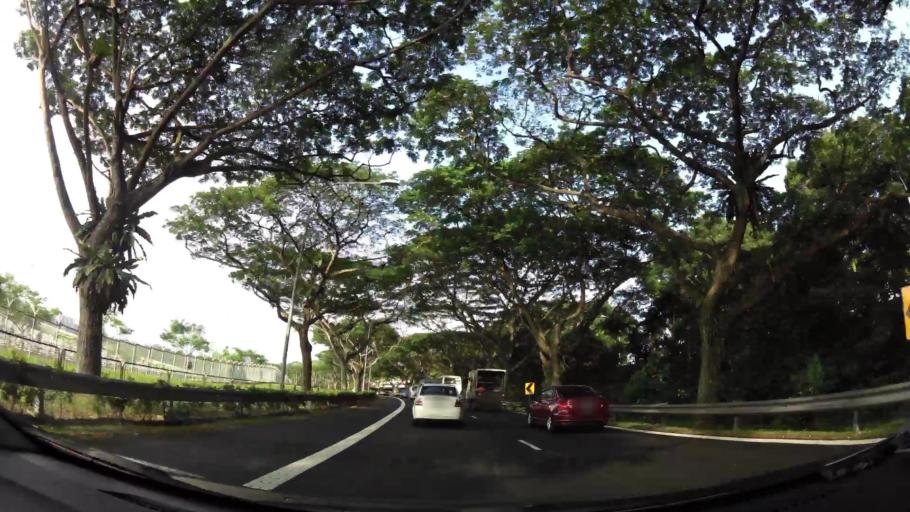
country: MY
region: Johor
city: Johor Bahru
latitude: 1.3626
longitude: 103.7069
